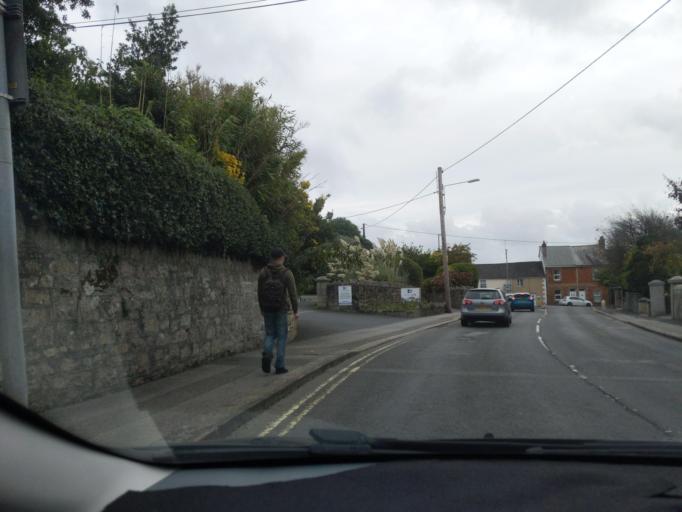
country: GB
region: England
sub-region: Cornwall
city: St Austell
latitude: 50.3388
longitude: -4.7871
